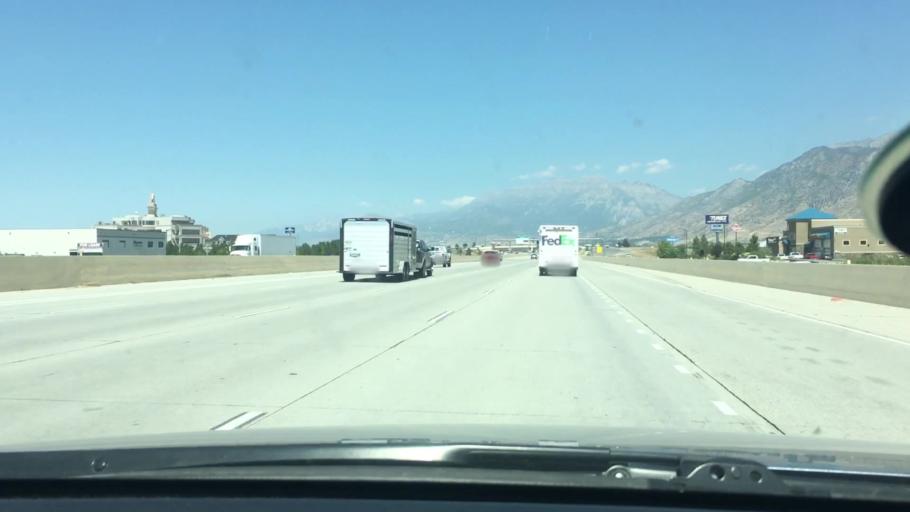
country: US
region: Utah
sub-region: Utah County
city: Springville
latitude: 40.1544
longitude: -111.6465
